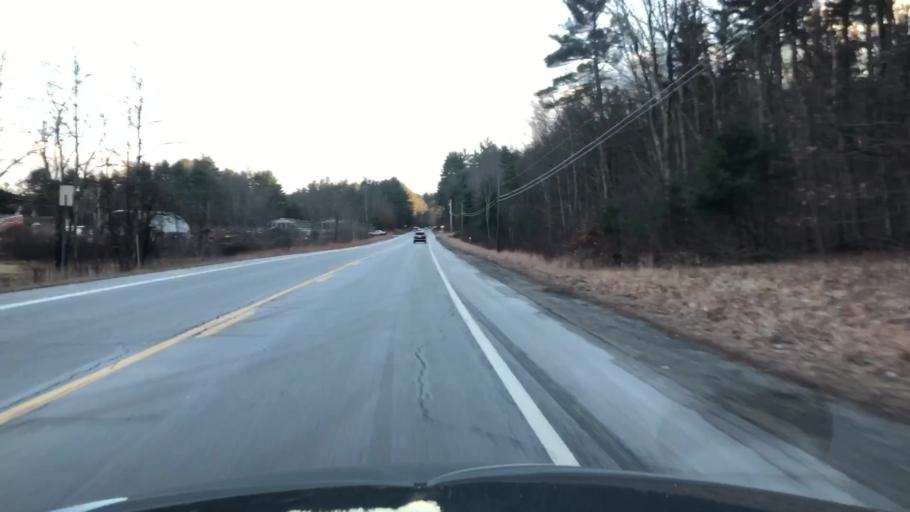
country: US
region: New Hampshire
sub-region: Hillsborough County
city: Brookline
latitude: 42.7227
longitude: -71.6625
